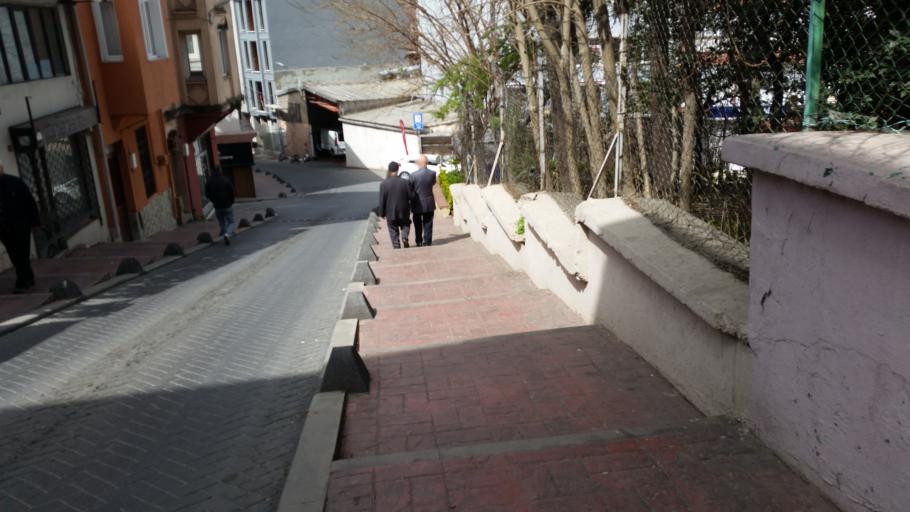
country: TR
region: Istanbul
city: Eminoenue
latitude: 41.0325
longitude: 28.9705
